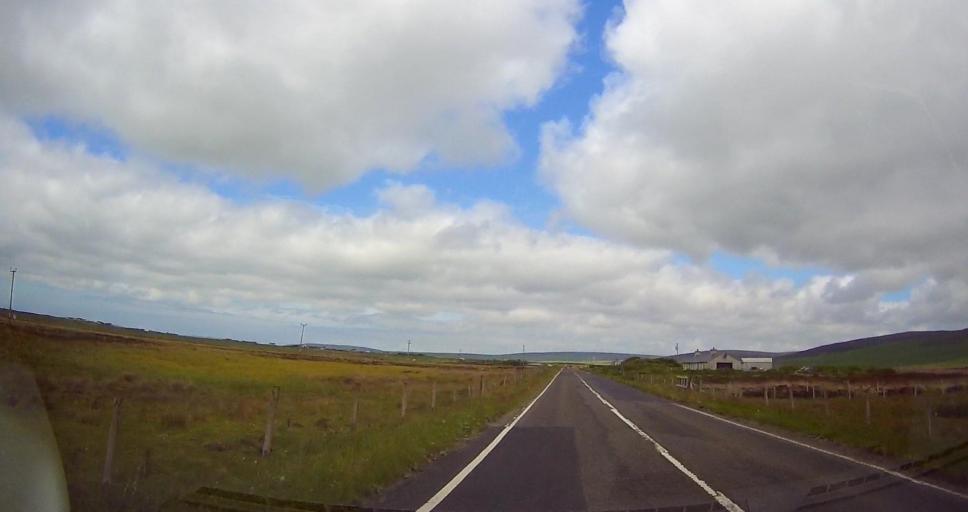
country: GB
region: Scotland
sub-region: Orkney Islands
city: Stromness
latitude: 59.0128
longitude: -3.1560
